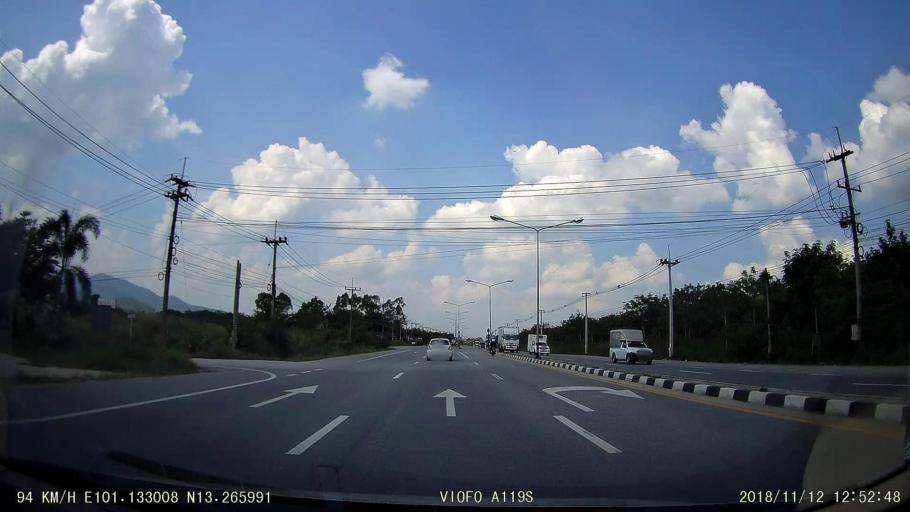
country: TH
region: Chon Buri
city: Ban Bueng
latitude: 13.2662
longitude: 101.1329
